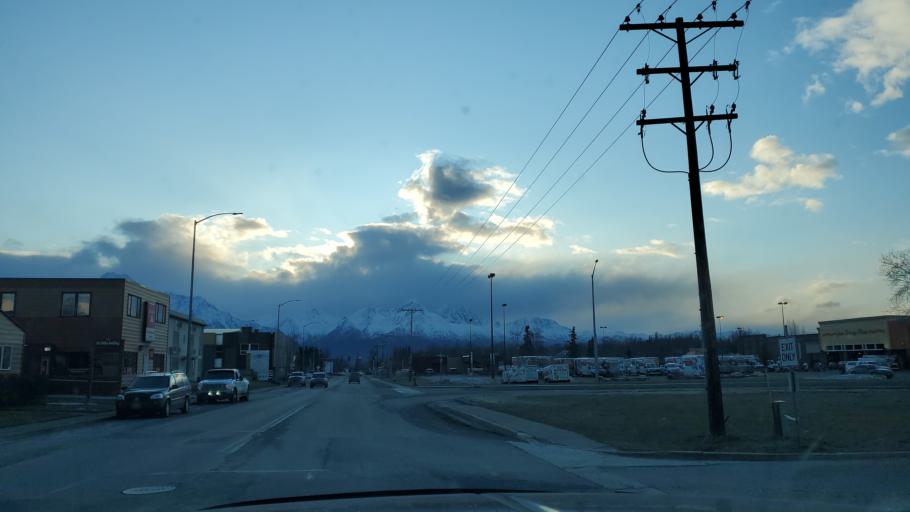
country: US
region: Alaska
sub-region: Matanuska-Susitna Borough
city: Palmer
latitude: 61.6020
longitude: -149.1183
